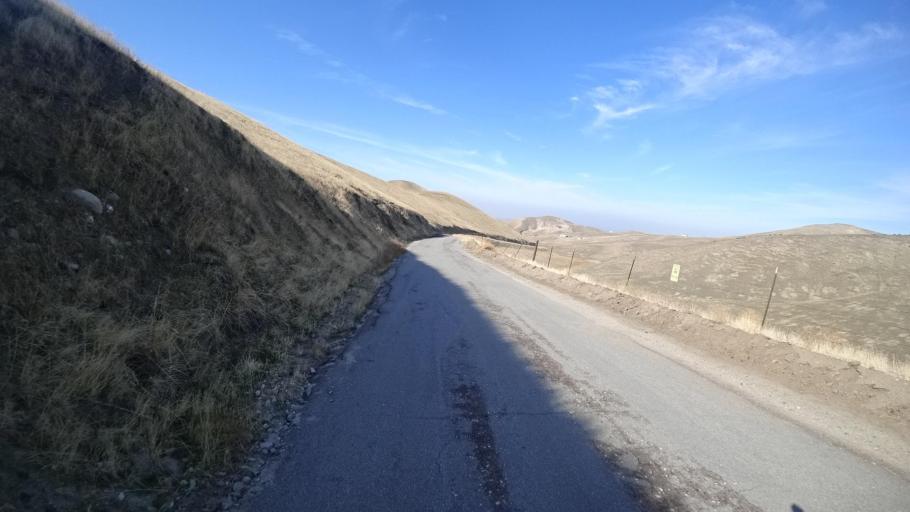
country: US
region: California
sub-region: Kern County
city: Lamont
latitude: 35.4011
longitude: -118.7828
